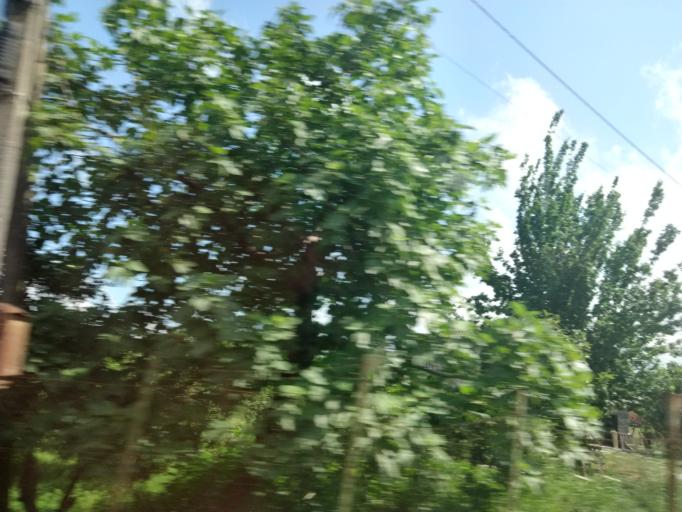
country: GE
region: Ajaria
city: Batumi
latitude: 41.5846
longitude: 41.6031
